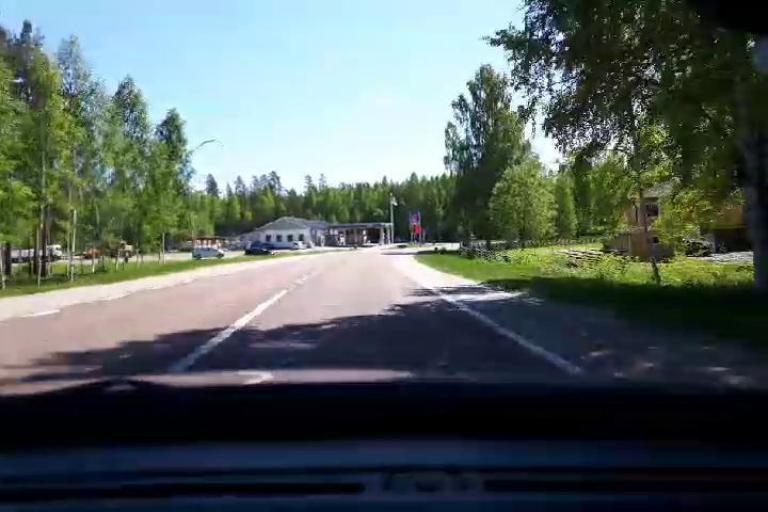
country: SE
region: Jaemtland
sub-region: Harjedalens Kommun
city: Sveg
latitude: 62.1718
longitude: 14.9502
